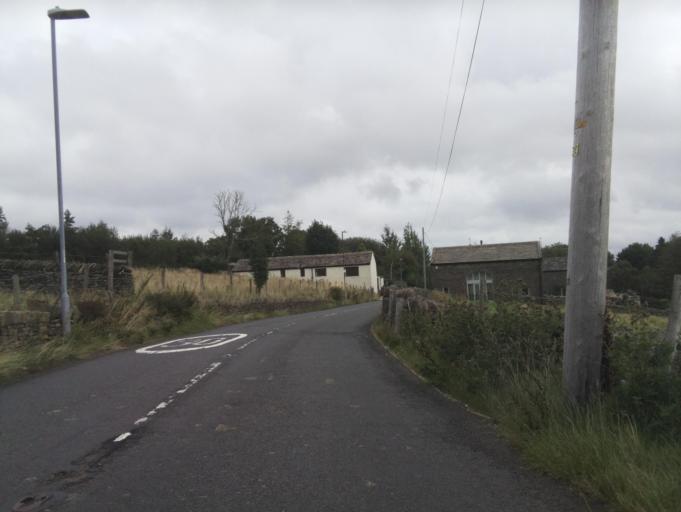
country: GB
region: England
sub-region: Kirklees
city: Meltham
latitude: 53.5463
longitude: -1.8473
